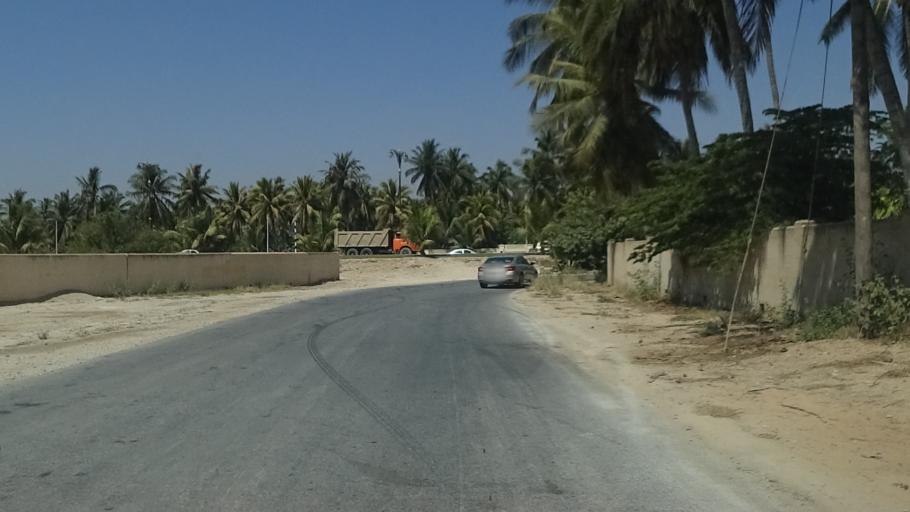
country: OM
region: Zufar
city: Salalah
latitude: 17.0236
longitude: 54.1229
